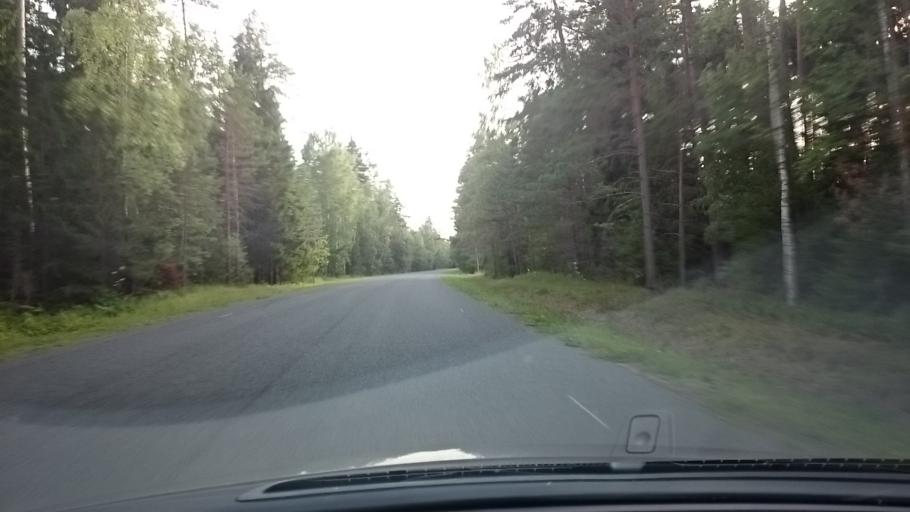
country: EE
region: Saare
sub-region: Kuressaare linn
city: Kuressaare
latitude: 58.4399
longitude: 22.2307
